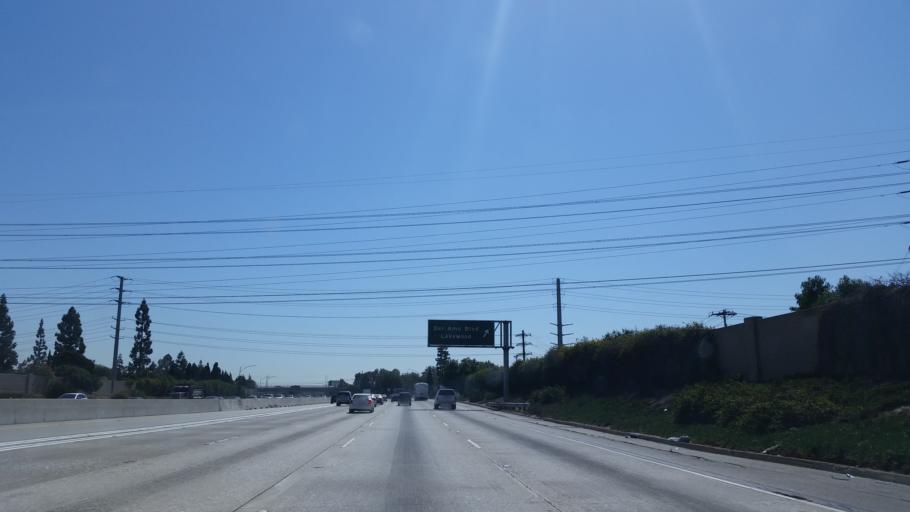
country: US
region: California
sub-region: Los Angeles County
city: Artesia
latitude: 33.8511
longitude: -118.0946
